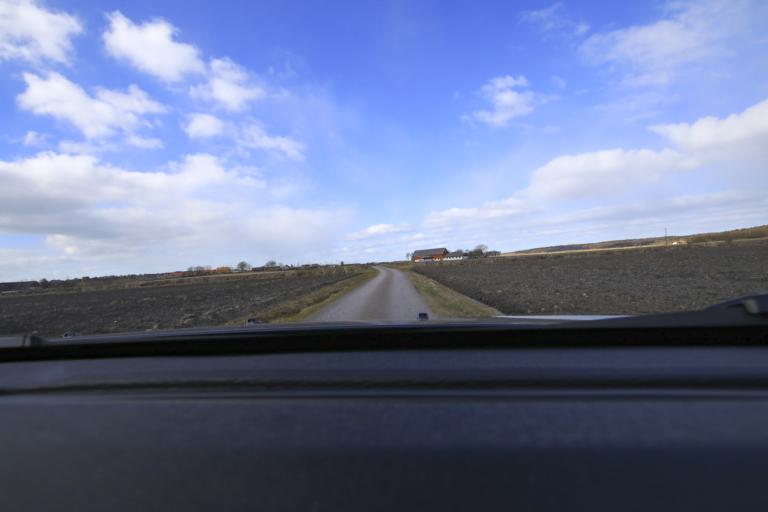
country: SE
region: Halland
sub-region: Kungsbacka Kommun
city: Frillesas
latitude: 57.2325
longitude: 12.1533
